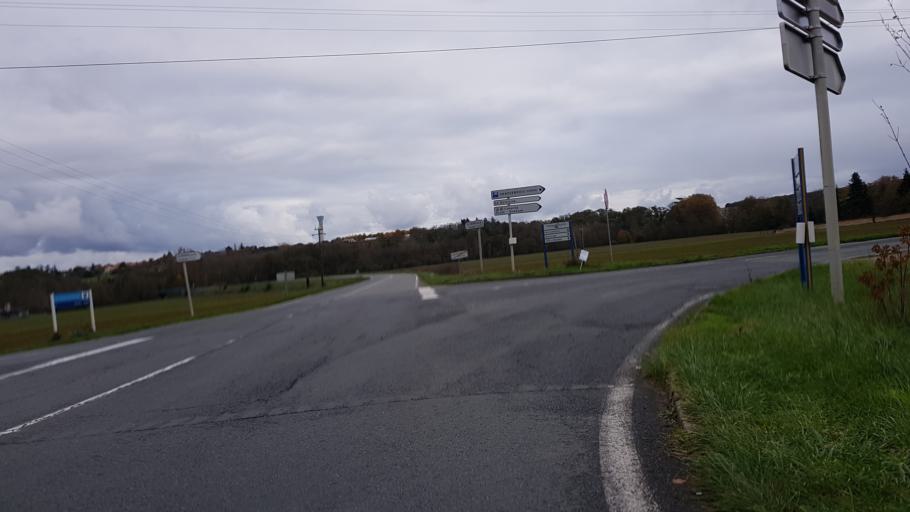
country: FR
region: Poitou-Charentes
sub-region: Departement de la Vienne
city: Chasseneuil-du-Poitou
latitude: 46.6634
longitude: 0.3802
